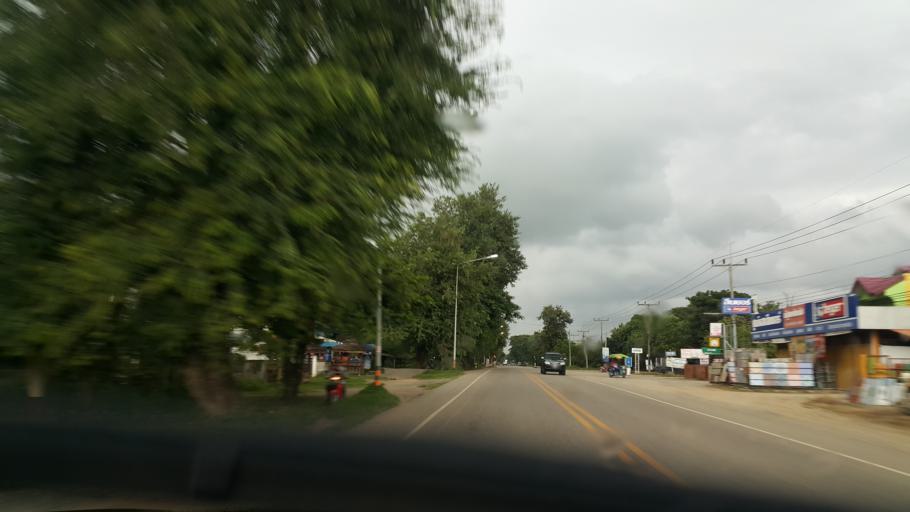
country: TH
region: Phayao
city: Phu Kam Yao
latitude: 19.2371
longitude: 100.0486
